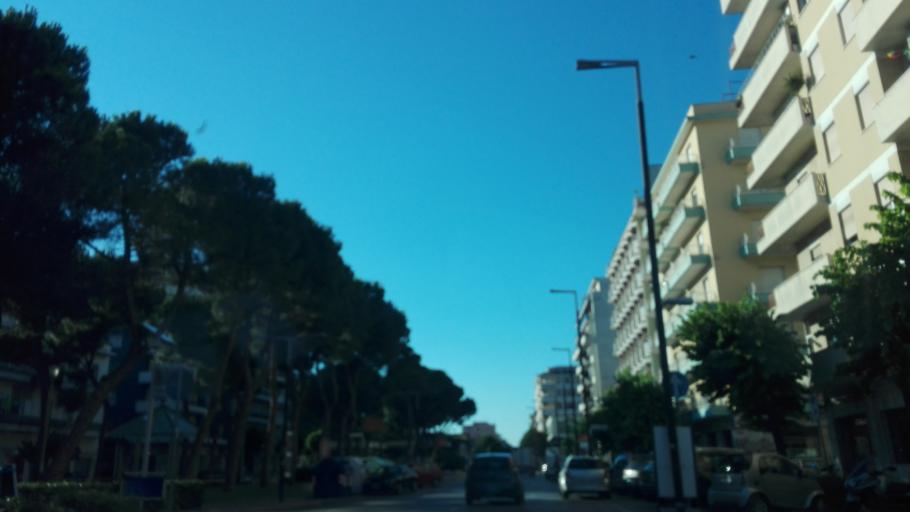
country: IT
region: Abruzzo
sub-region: Provincia di Pescara
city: Pescara
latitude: 42.4818
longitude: 14.1920
